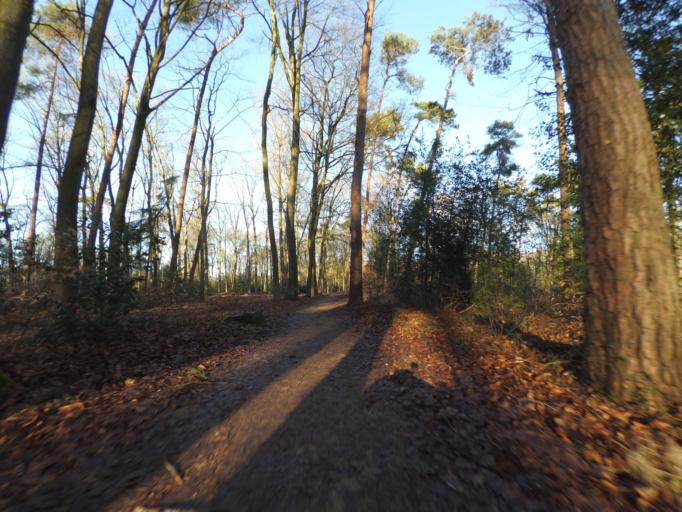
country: NL
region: Gelderland
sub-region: Gemeente Putten
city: Putten
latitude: 52.2692
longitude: 5.5995
